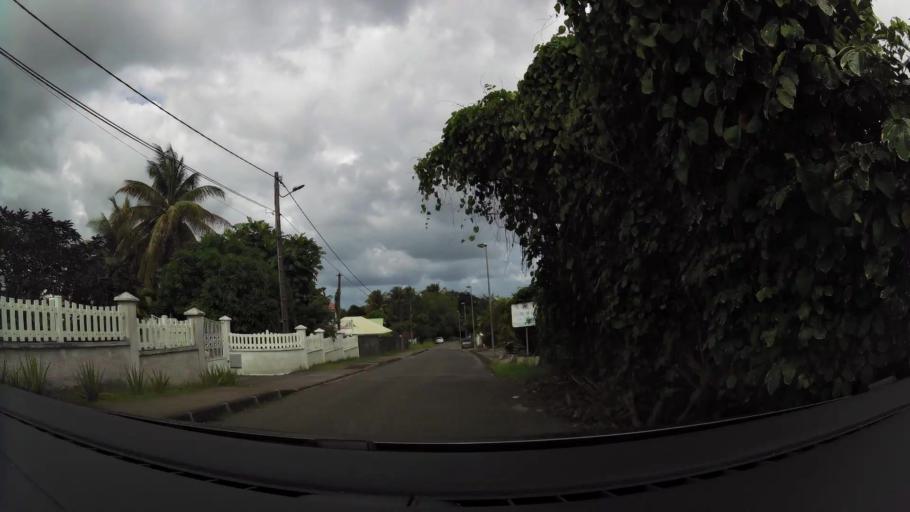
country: GP
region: Guadeloupe
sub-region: Guadeloupe
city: Baie-Mahault
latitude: 16.2576
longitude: -61.5798
